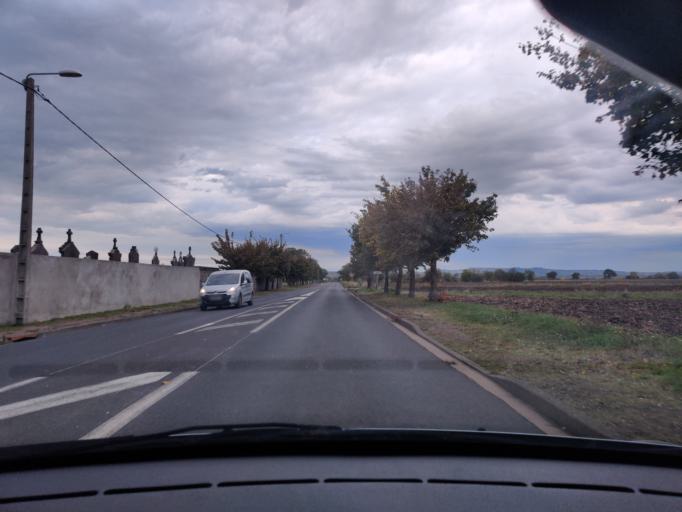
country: FR
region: Auvergne
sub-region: Departement du Puy-de-Dome
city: Saint-Bonnet-pres-Riom
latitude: 45.9321
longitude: 3.1115
